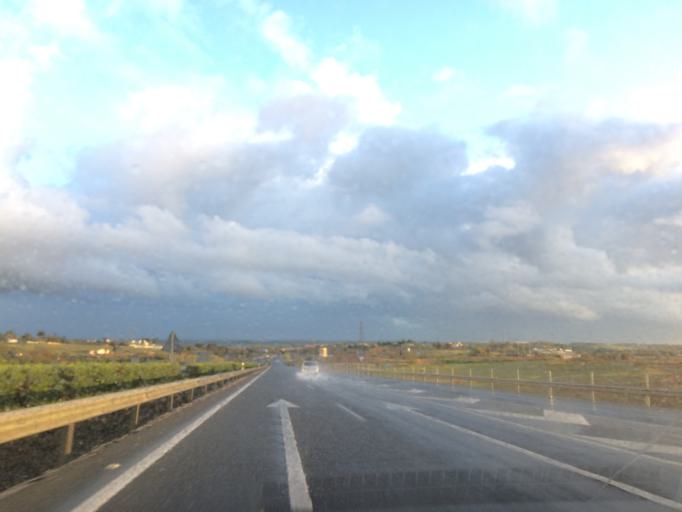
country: ES
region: Andalusia
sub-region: Provincia de Sevilla
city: Alcala de Guadaira
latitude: 37.3412
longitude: -5.8212
